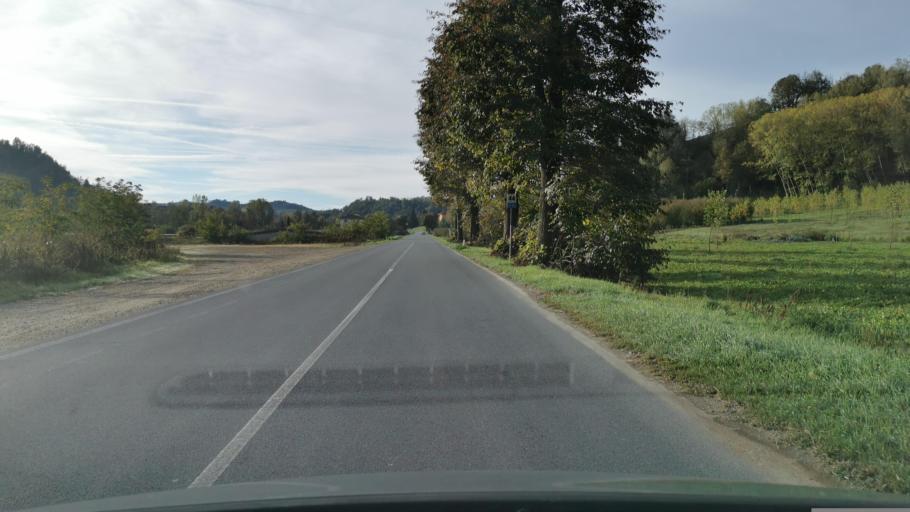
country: IT
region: Piedmont
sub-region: Provincia di Cuneo
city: Monchiero Borgonuovo
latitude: 44.5579
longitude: 7.9226
